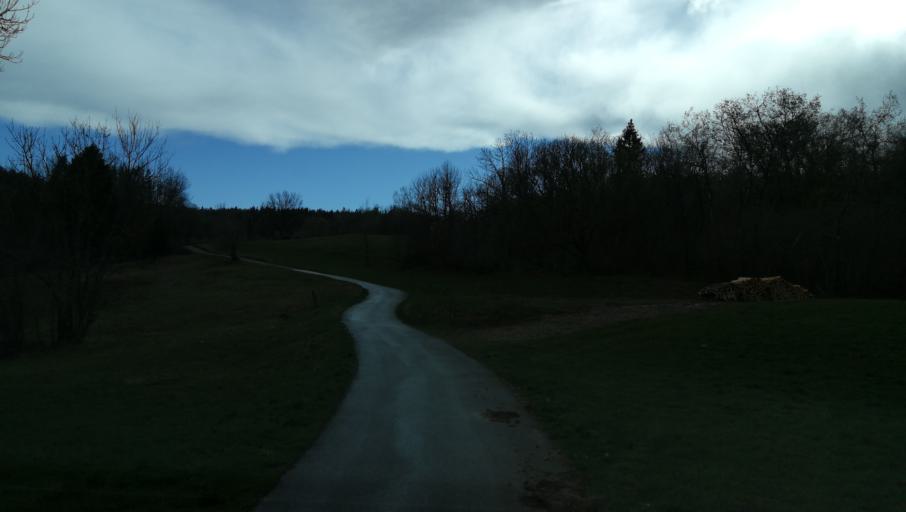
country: FR
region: Franche-Comte
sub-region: Departement du Jura
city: Lavans-les-Saint-Claude
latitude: 46.3174
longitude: 5.8078
